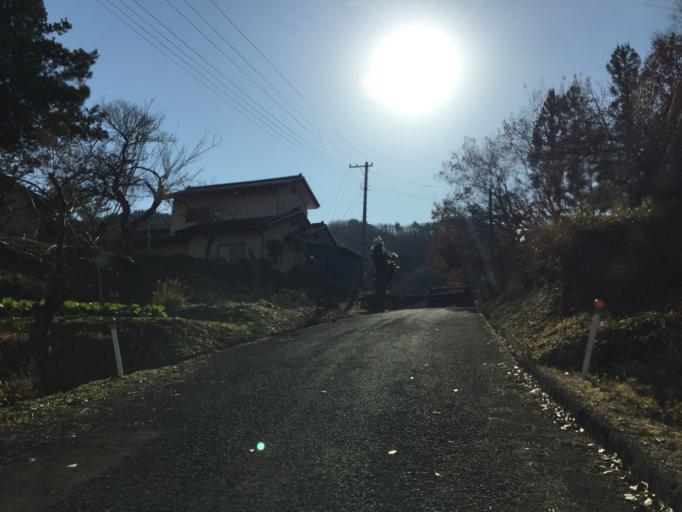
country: JP
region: Fukushima
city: Fukushima-shi
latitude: 37.7006
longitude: 140.5290
